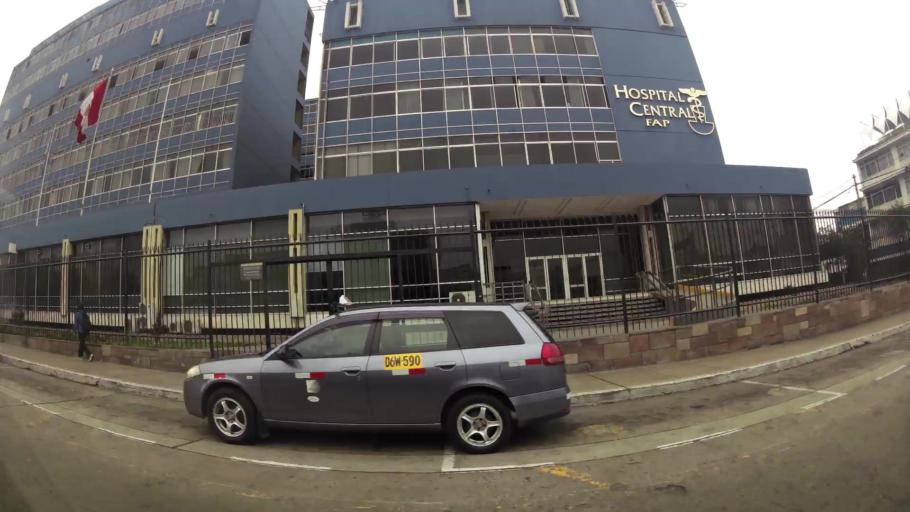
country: PE
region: Lima
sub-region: Lima
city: San Isidro
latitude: -12.1034
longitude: -77.0302
